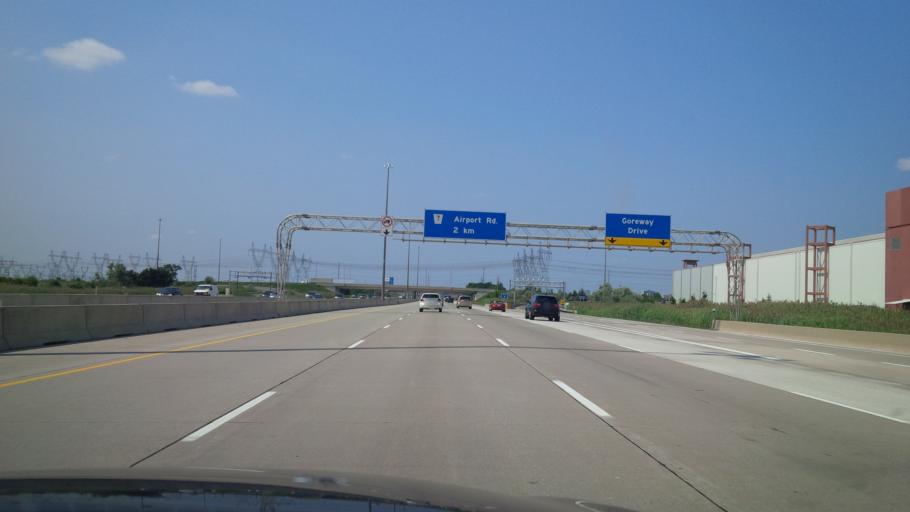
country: CA
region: Ontario
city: Brampton
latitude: 43.7387
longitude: -79.6570
